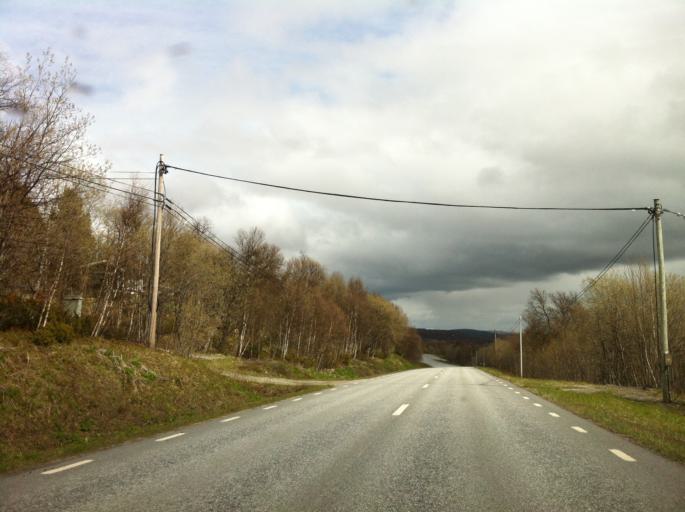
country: NO
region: Sor-Trondelag
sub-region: Tydal
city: Aas
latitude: 62.5533
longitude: 12.2855
